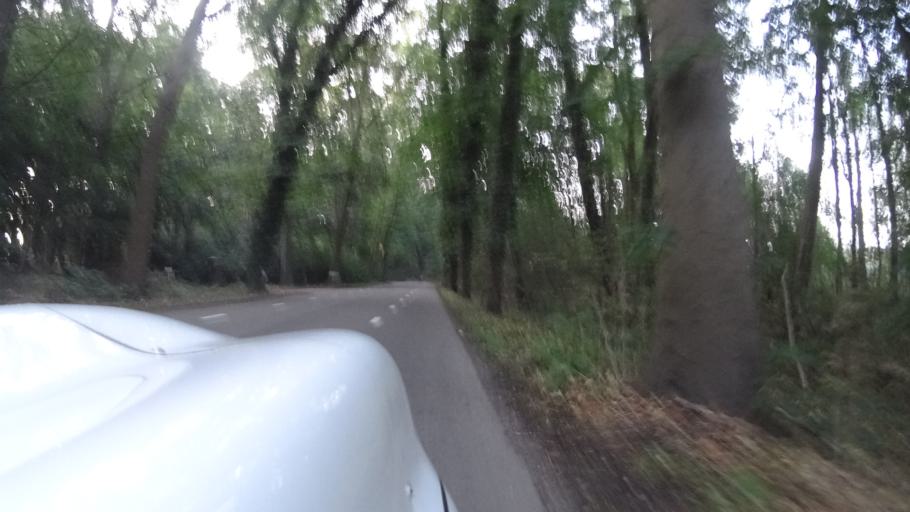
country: NL
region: Limburg
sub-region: Gemeente Venray
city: Venray
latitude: 51.5574
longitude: 6.0446
